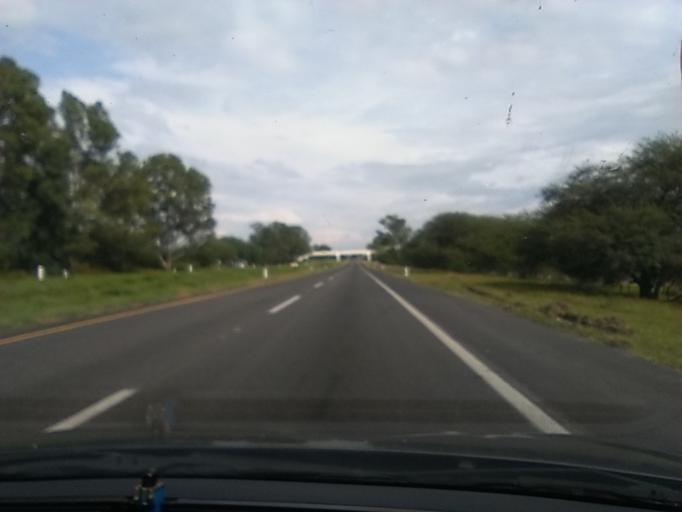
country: MX
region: Jalisco
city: La Barca
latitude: 20.3370
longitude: -102.5995
